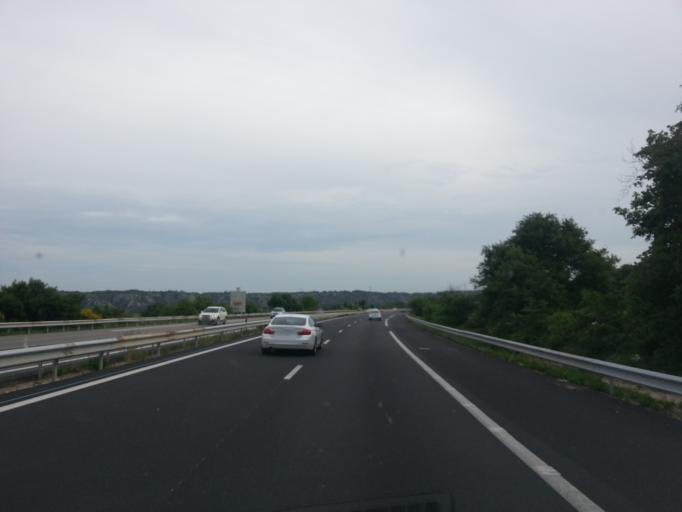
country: FR
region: Languedoc-Roussillon
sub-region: Departement du Gard
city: Roquemaure
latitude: 44.0434
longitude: 4.7652
